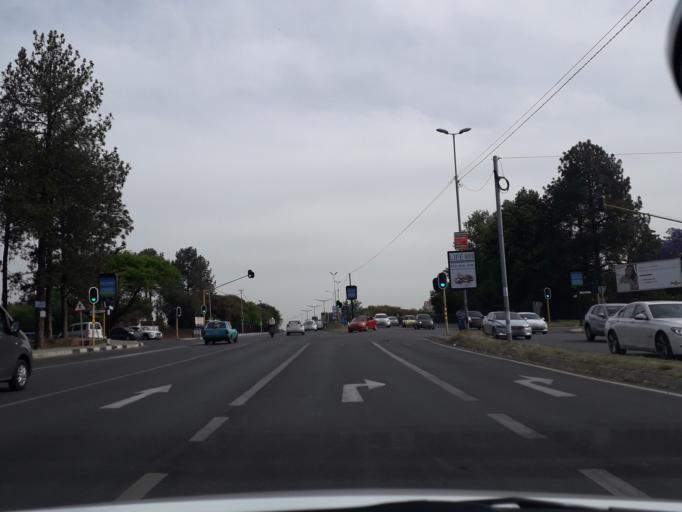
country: ZA
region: Gauteng
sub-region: City of Johannesburg Metropolitan Municipality
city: Diepsloot
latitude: -26.0388
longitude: 28.0257
